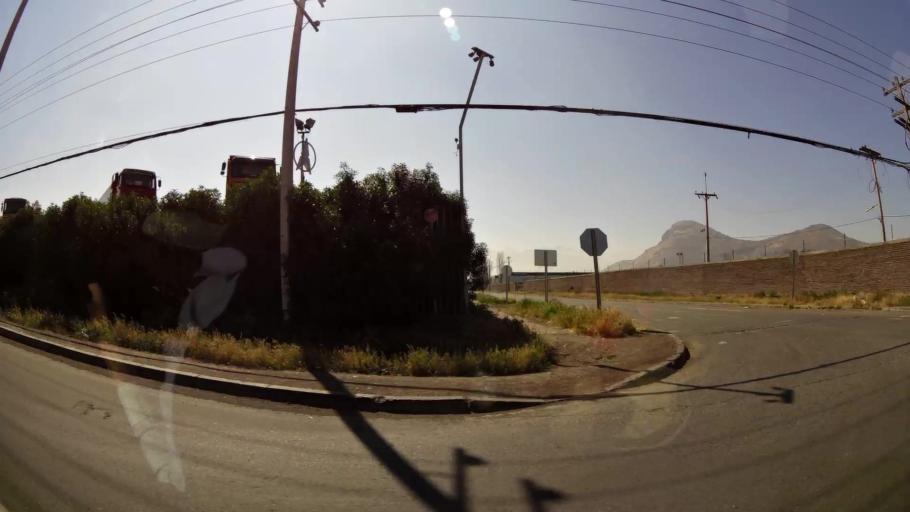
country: CL
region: Santiago Metropolitan
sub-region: Provincia de Chacabuco
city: Chicureo Abajo
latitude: -33.3104
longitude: -70.7248
